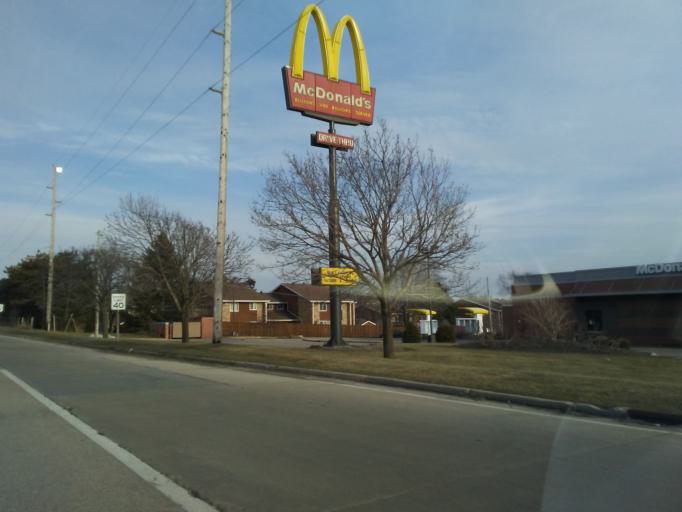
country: US
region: Wisconsin
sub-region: Iowa County
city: Dodgeville
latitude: 42.9726
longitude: -90.1325
